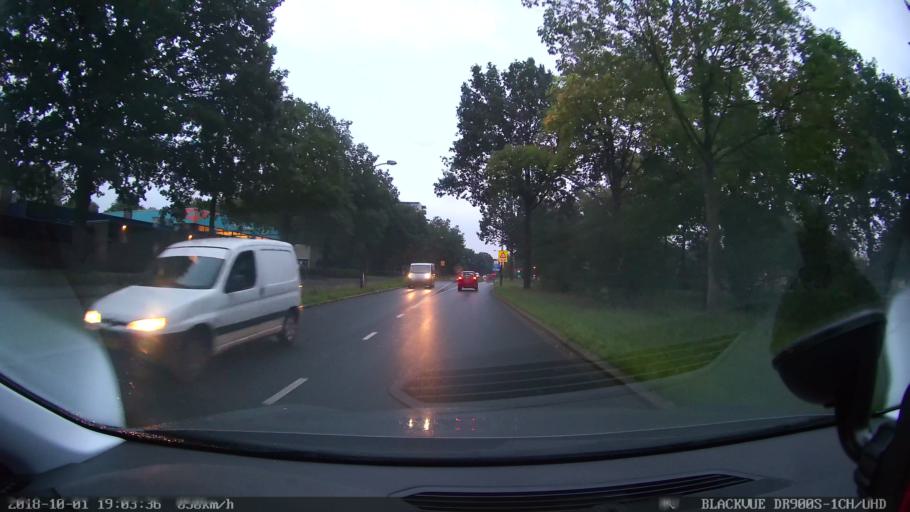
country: NL
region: Gelderland
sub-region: Gemeente Apeldoorn
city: Apeldoorn
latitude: 52.2278
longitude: 5.9930
